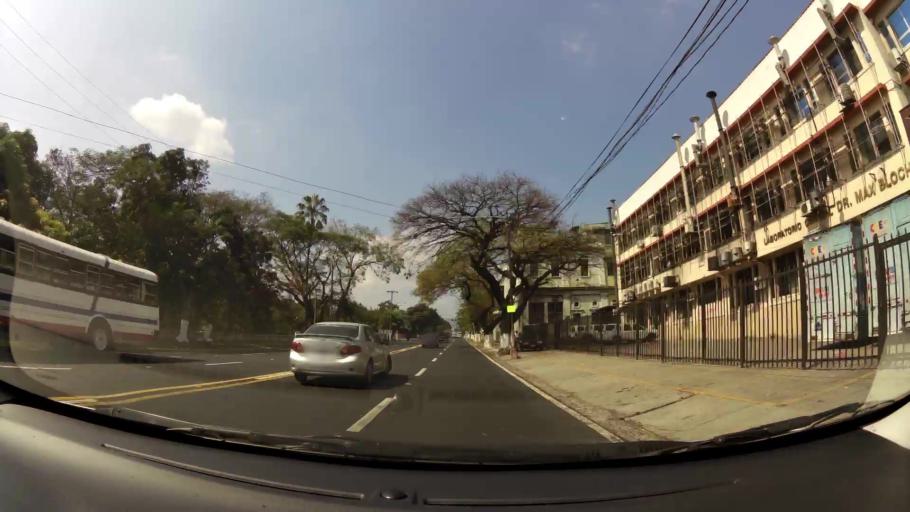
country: SV
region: San Salvador
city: San Salvador
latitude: 13.6998
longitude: -89.2076
